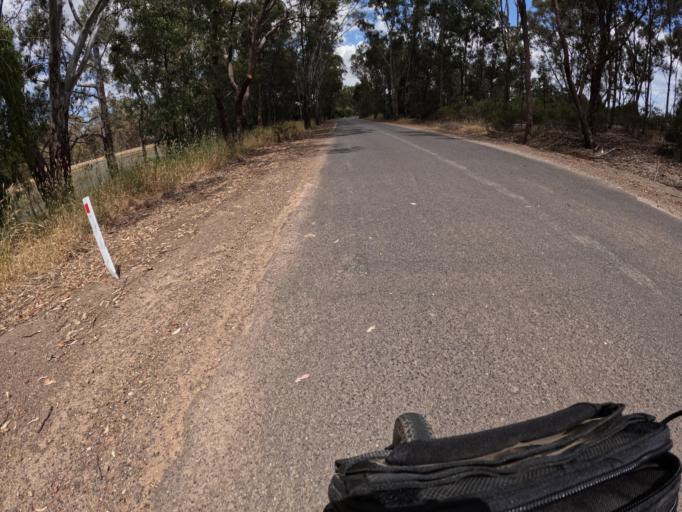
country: AU
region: Victoria
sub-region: Greater Shepparton
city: Shepparton
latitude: -36.6934
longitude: 145.1743
